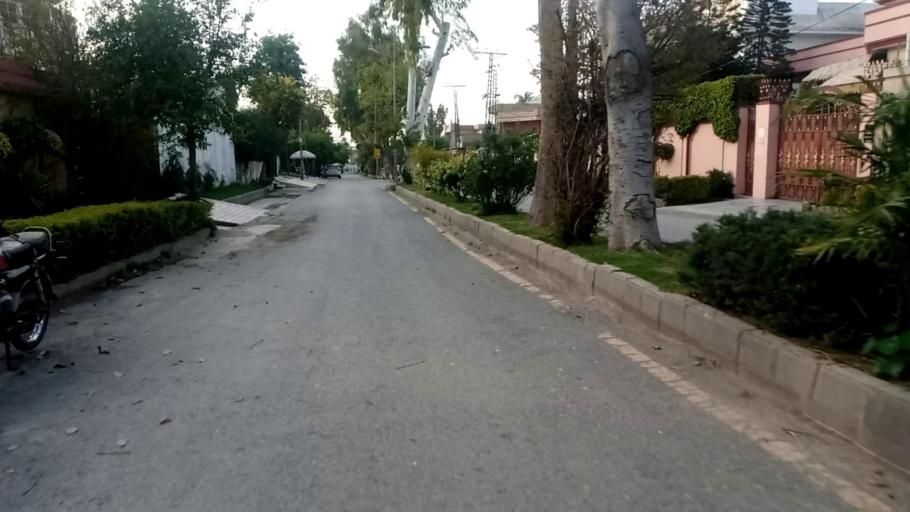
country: PK
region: Khyber Pakhtunkhwa
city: Peshawar
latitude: 34.0217
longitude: 71.5508
